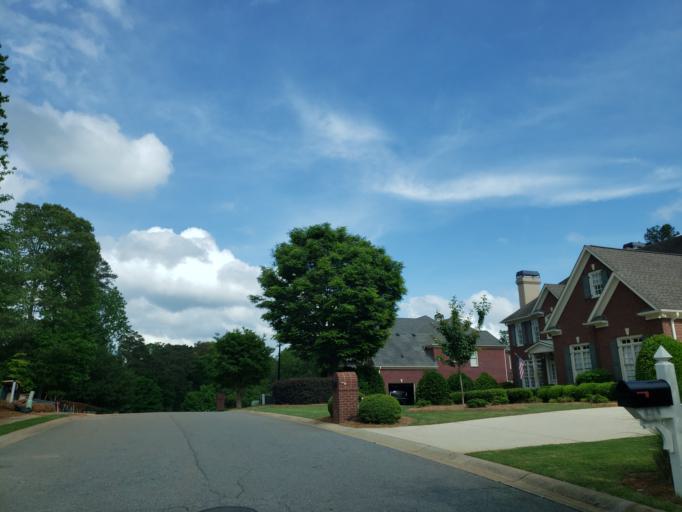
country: US
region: Georgia
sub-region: Cobb County
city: Marietta
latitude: 33.9602
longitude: -84.5724
